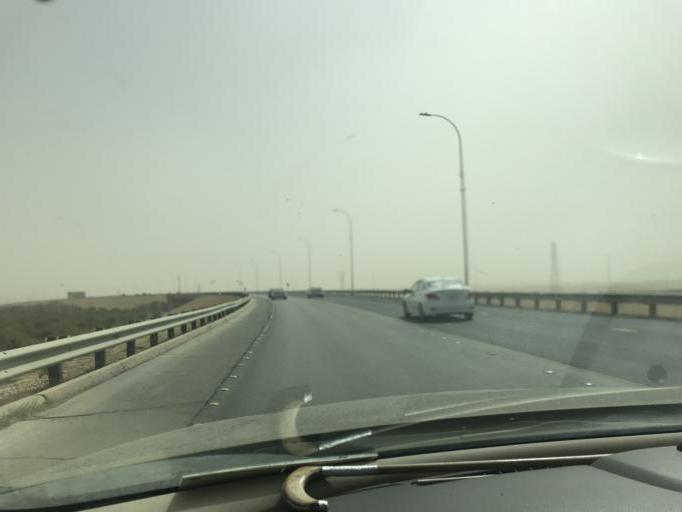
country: SA
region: Ar Riyad
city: Riyadh
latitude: 24.9037
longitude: 46.7104
